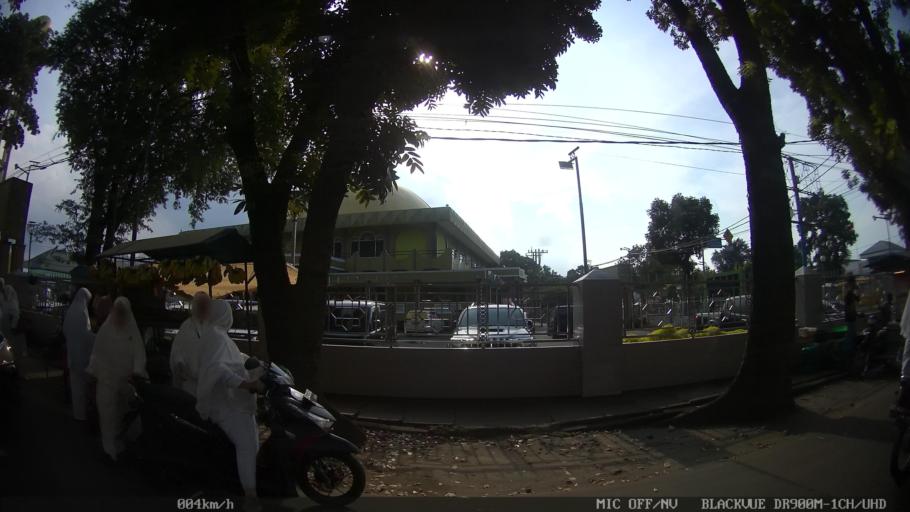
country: ID
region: North Sumatra
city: Binjai
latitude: 3.6082
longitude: 98.4978
